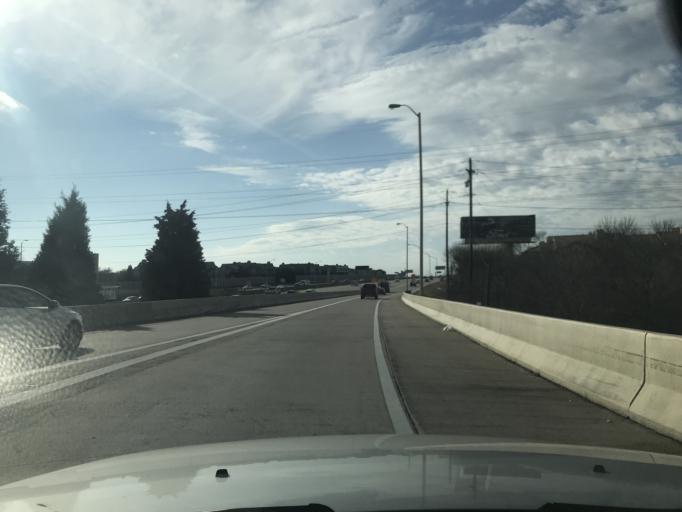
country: US
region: Texas
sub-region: Dallas County
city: Addison
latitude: 33.0133
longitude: -96.8310
